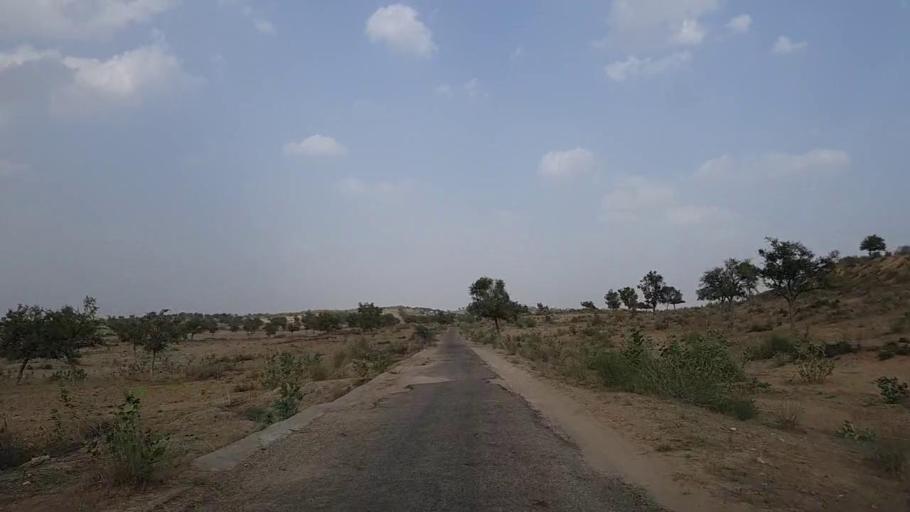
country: PK
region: Sindh
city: Islamkot
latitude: 24.7668
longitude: 70.1563
